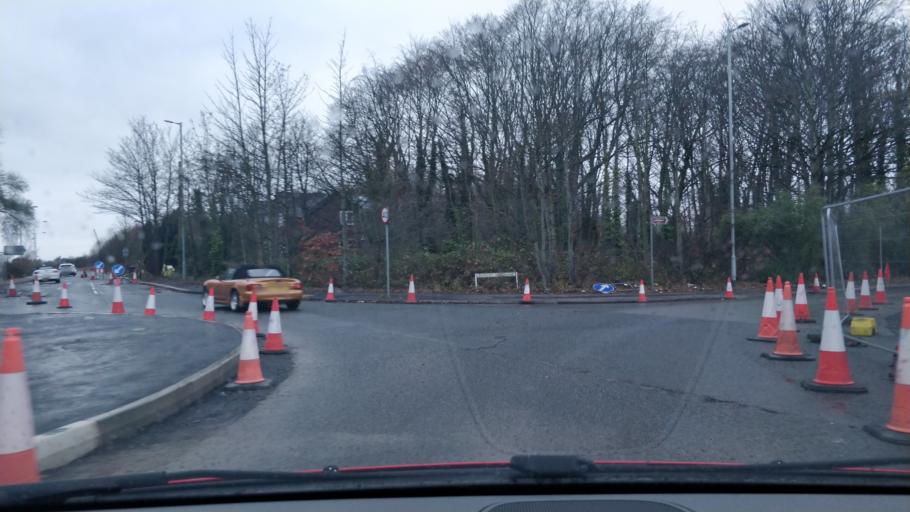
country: GB
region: England
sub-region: Sefton
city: Thornton
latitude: 53.4908
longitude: -2.9888
